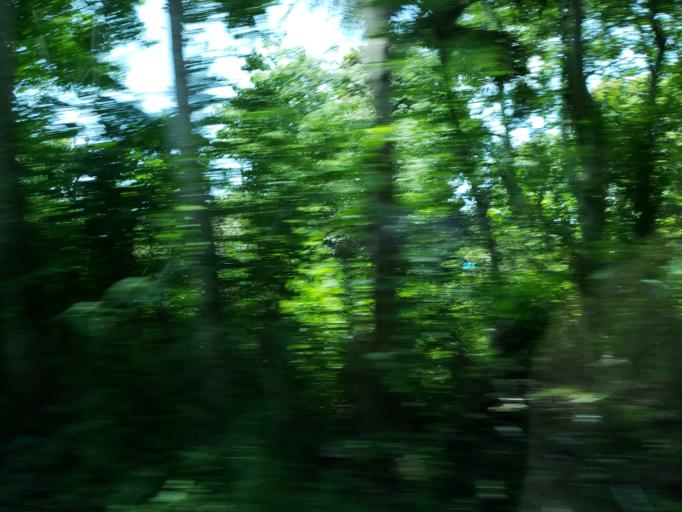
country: ID
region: Bali
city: Kangin
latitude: -8.8330
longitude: 115.1363
